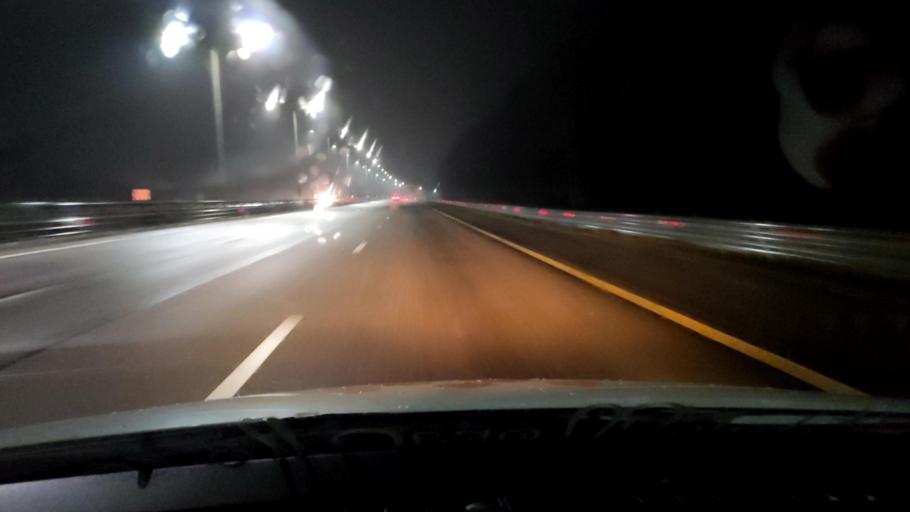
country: RU
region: Voronezj
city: Podgornoye
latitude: 51.8336
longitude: 39.2337
